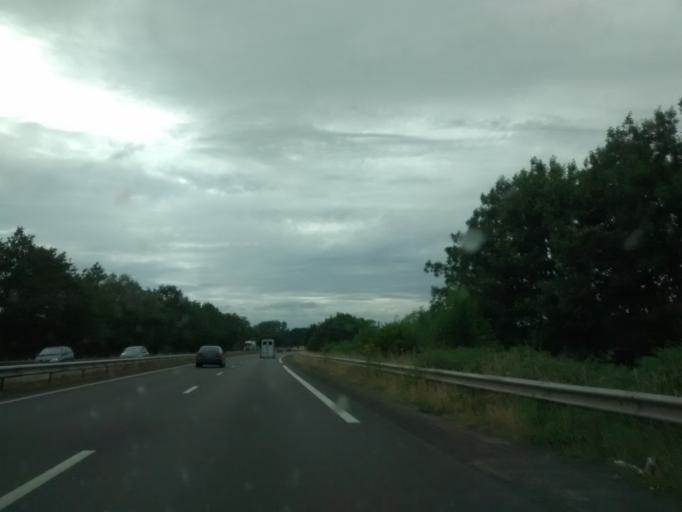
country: FR
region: Brittany
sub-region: Departement des Cotes-d'Armor
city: Broons
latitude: 48.2958
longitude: -2.2253
